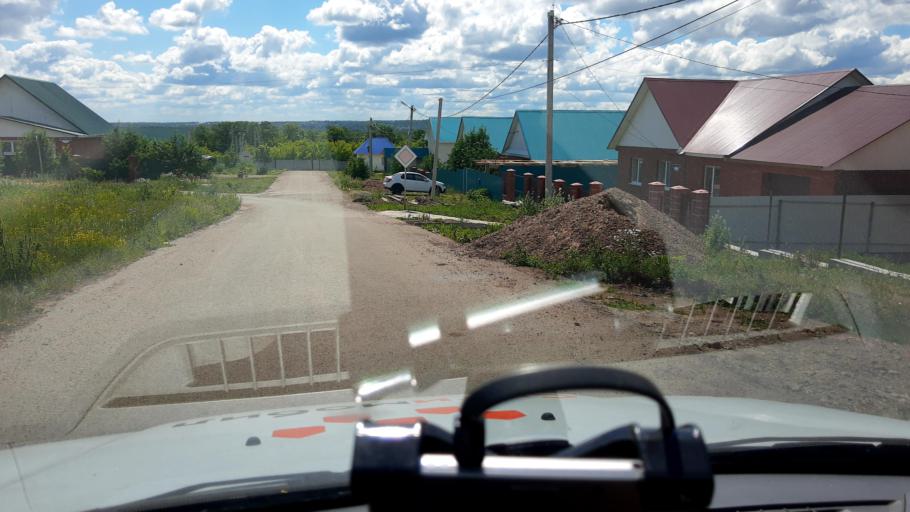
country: RU
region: Bashkortostan
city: Avdon
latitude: 54.6435
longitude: 55.7303
